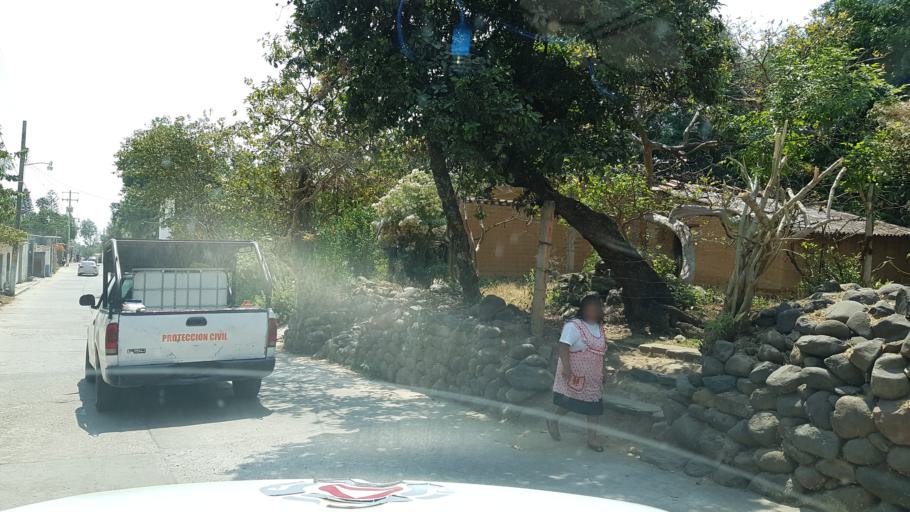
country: MX
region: Morelos
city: Ocuituco
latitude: 18.8849
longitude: -98.8163
